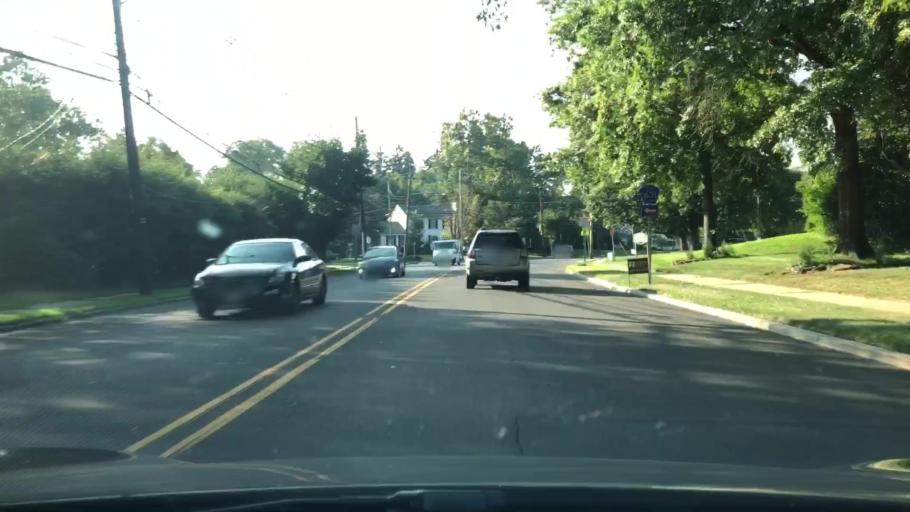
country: US
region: New Jersey
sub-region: Mercer County
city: Pennington
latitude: 40.3164
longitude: -74.7890
